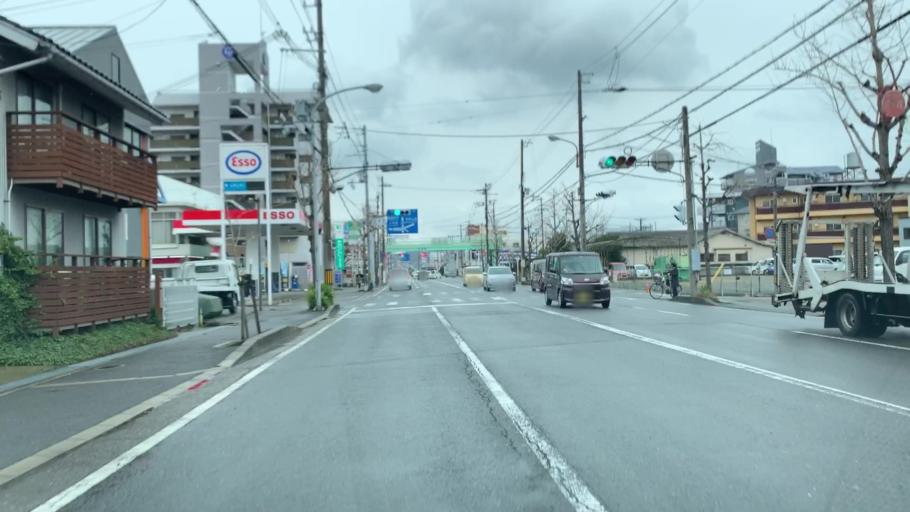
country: JP
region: Wakayama
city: Wakayama-shi
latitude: 34.2204
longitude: 135.1596
